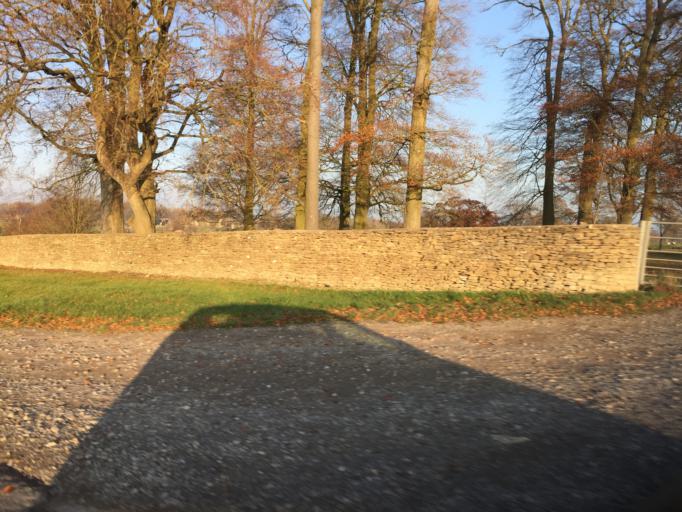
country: GB
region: England
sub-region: Wiltshire
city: Luckington
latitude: 51.5520
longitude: -2.2930
